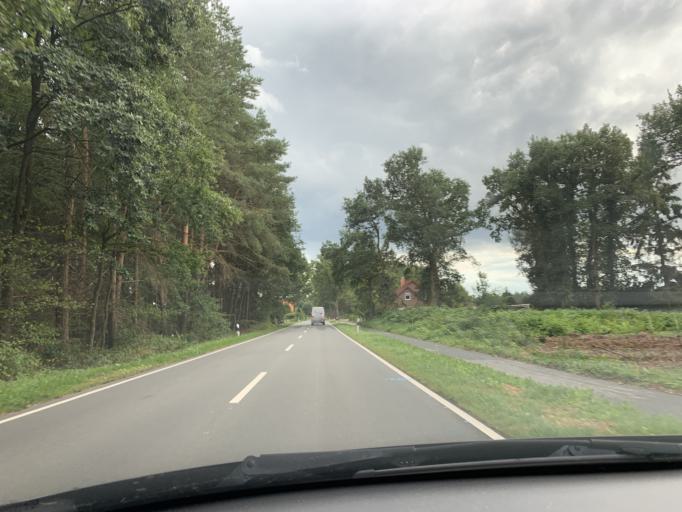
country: DE
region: Lower Saxony
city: Westerstede
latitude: 53.2950
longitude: 7.9198
